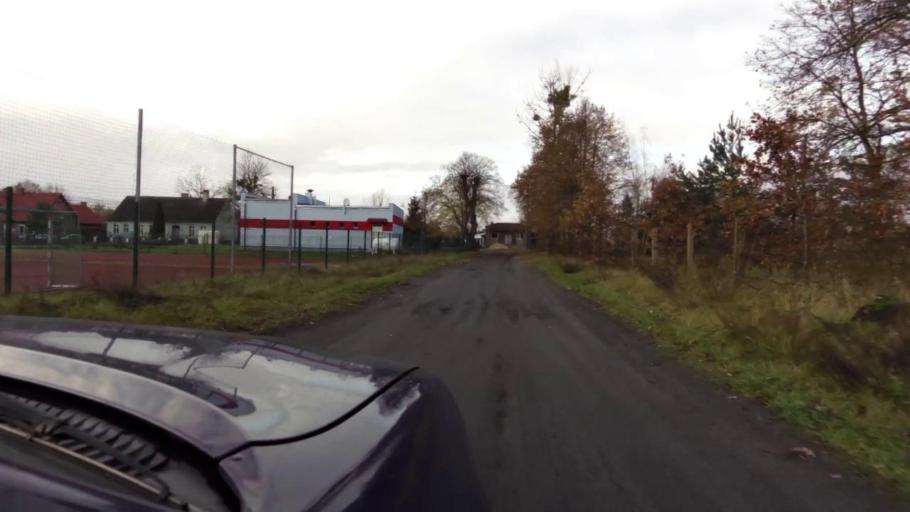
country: PL
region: West Pomeranian Voivodeship
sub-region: Powiat goleniowski
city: Goleniow
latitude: 53.5961
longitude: 14.7441
